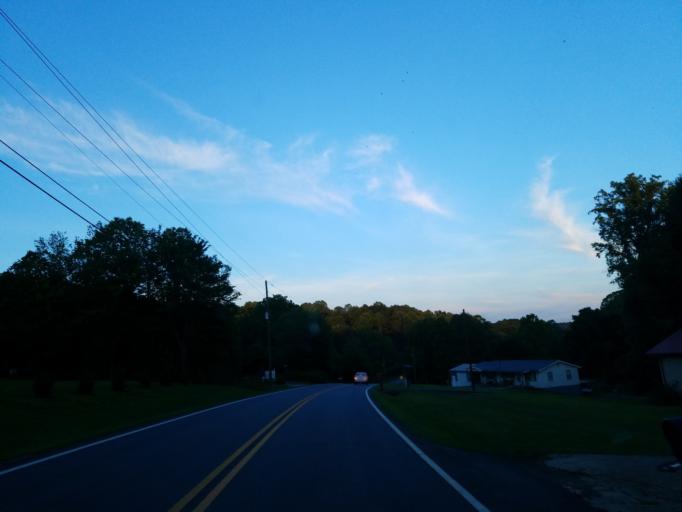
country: US
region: Georgia
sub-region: Lumpkin County
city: Dahlonega
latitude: 34.5633
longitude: -83.9400
